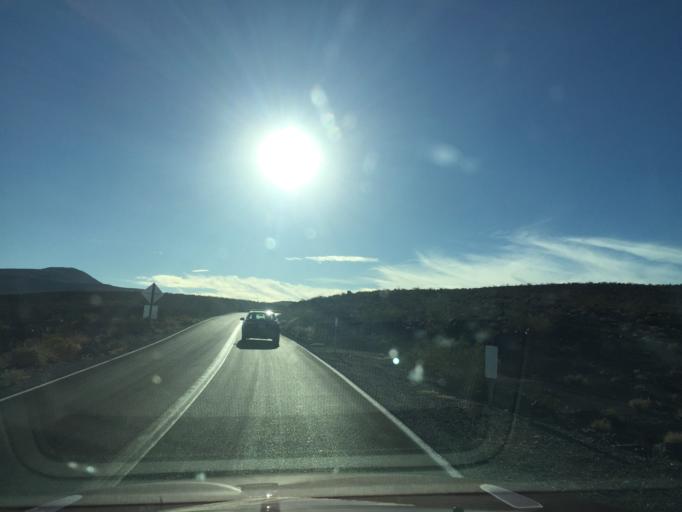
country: US
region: California
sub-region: Inyo County
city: Lone Pine
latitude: 36.3496
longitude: -117.5448
